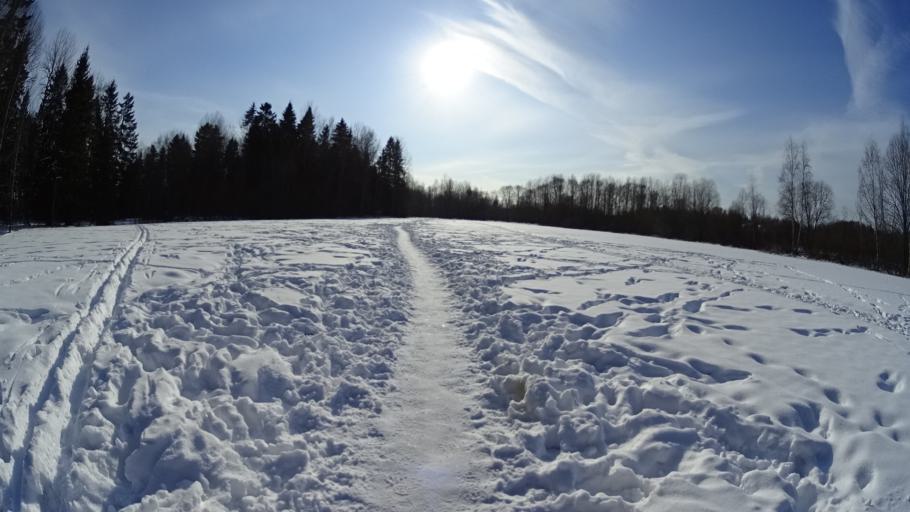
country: FI
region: Uusimaa
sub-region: Helsinki
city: Kauniainen
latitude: 60.2458
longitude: 24.7299
